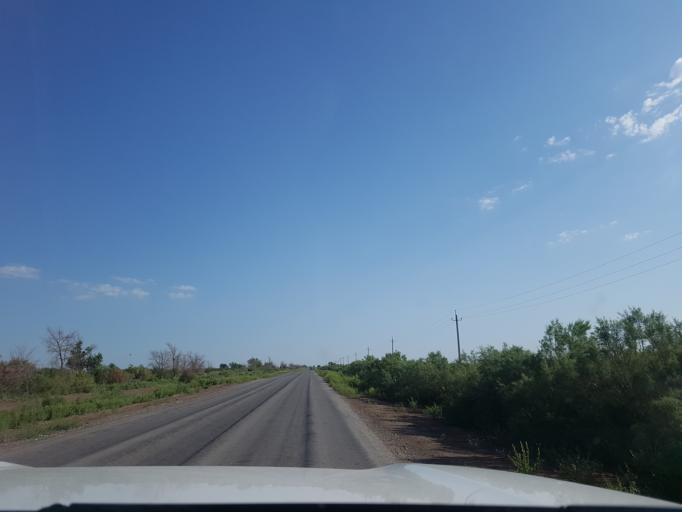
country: TM
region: Dasoguz
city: Koeneuergench
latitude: 41.8849
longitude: 58.7067
